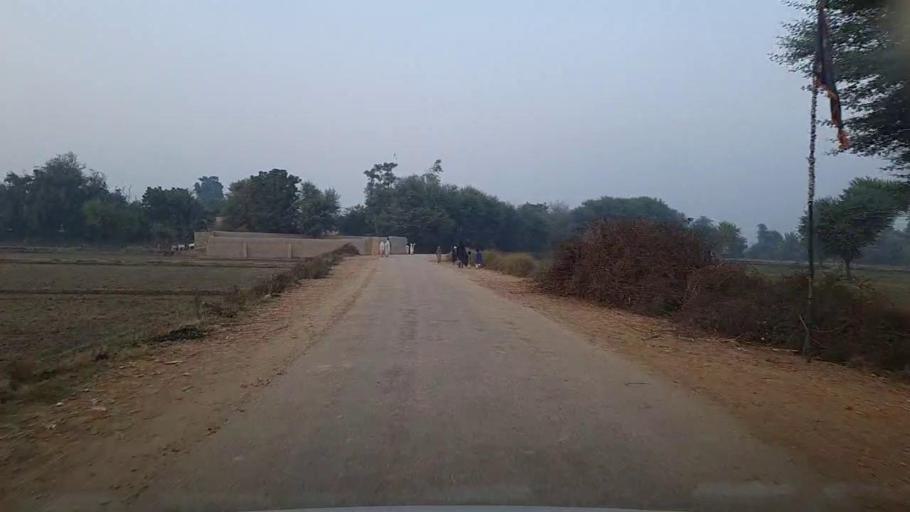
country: PK
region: Sindh
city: Bozdar
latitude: 27.0603
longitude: 68.5947
